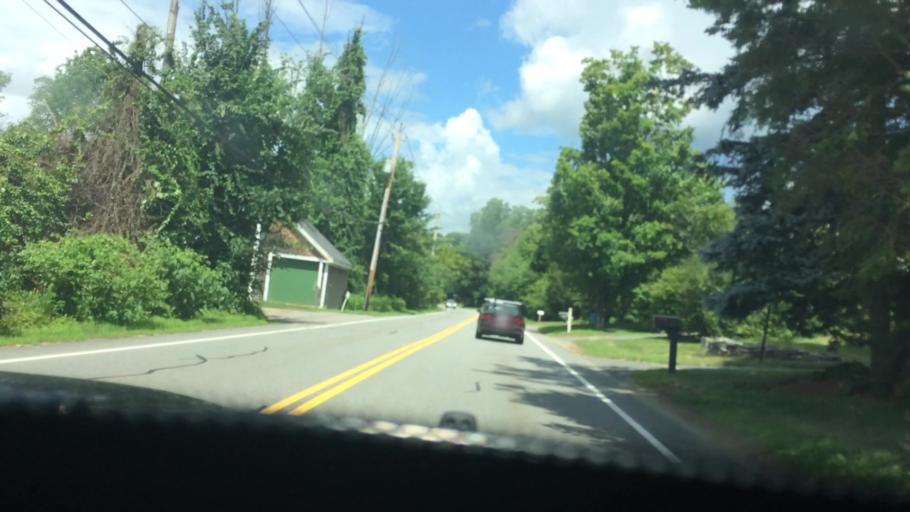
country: US
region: Massachusetts
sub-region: Middlesex County
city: Wayland
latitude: 42.3710
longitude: -71.3699
